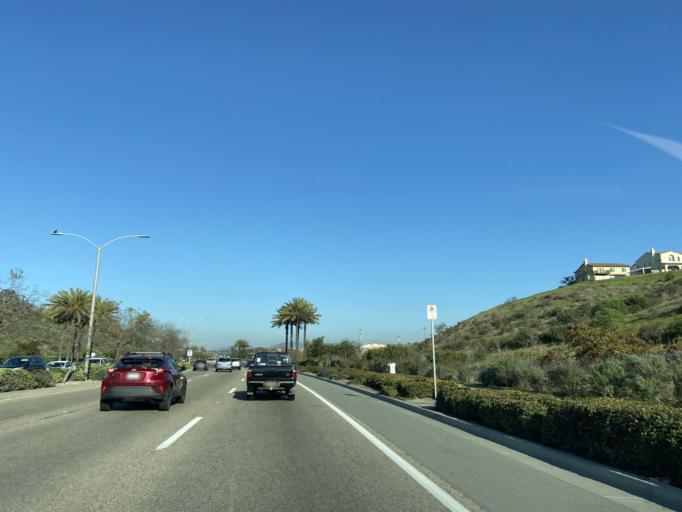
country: US
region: California
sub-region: San Diego County
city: Bonita
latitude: 32.6178
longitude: -116.9987
